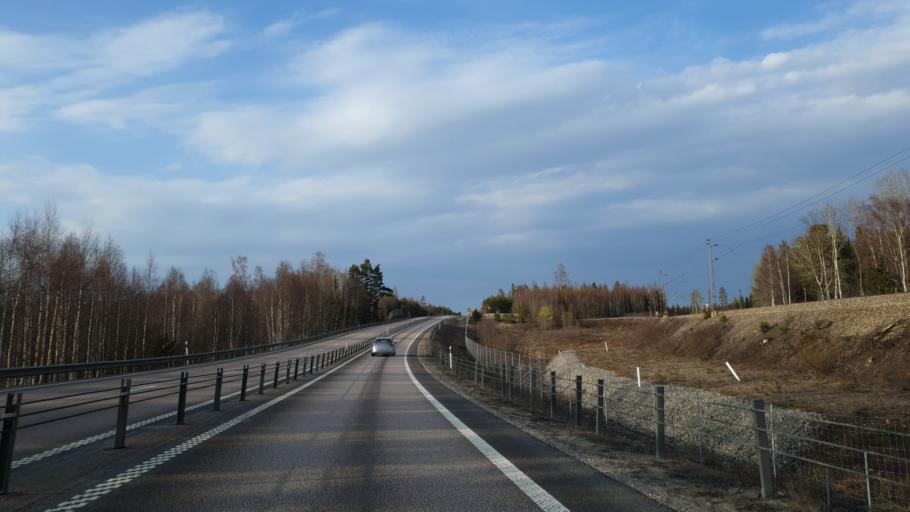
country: SE
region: Gaevleborg
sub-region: Hudiksvalls Kommun
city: Hudiksvall
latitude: 61.8335
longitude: 17.1925
